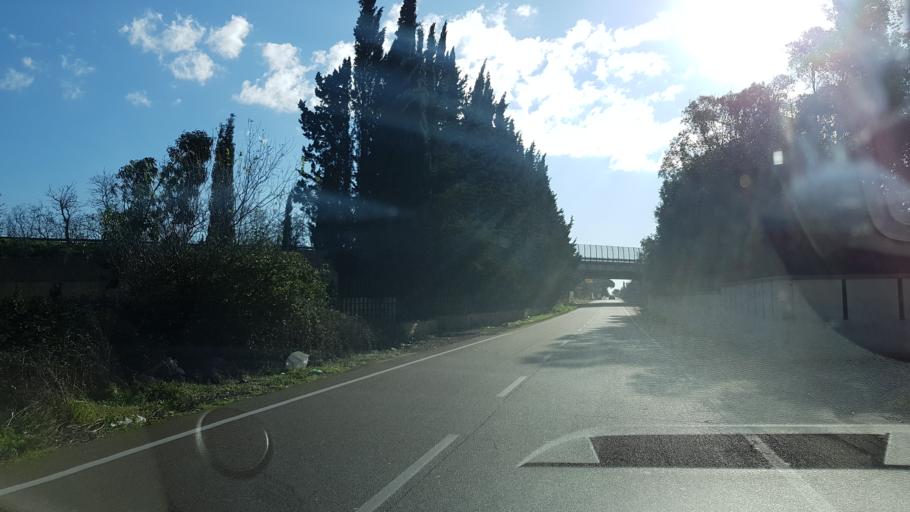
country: IT
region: Apulia
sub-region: Provincia di Lecce
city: Castromediano
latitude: 40.3270
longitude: 18.1843
